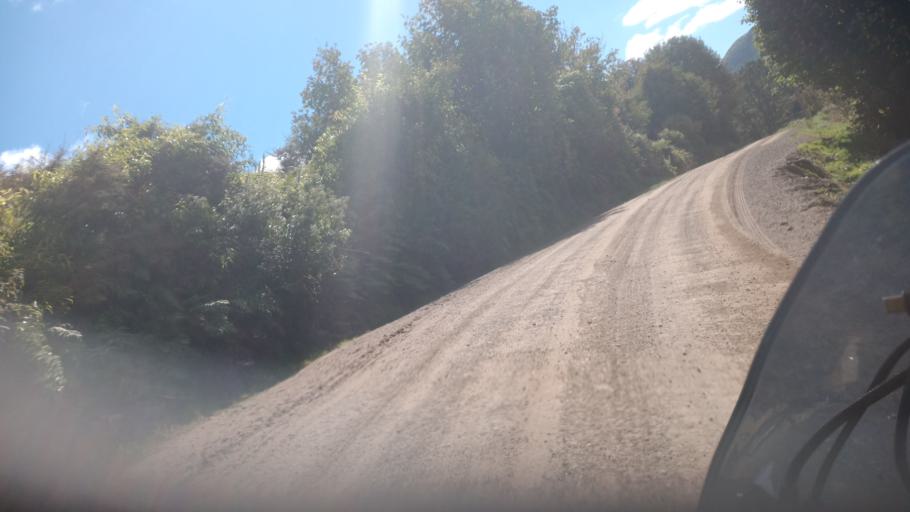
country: NZ
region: Bay of Plenty
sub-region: Opotiki District
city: Opotiki
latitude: -38.3335
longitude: 177.5771
